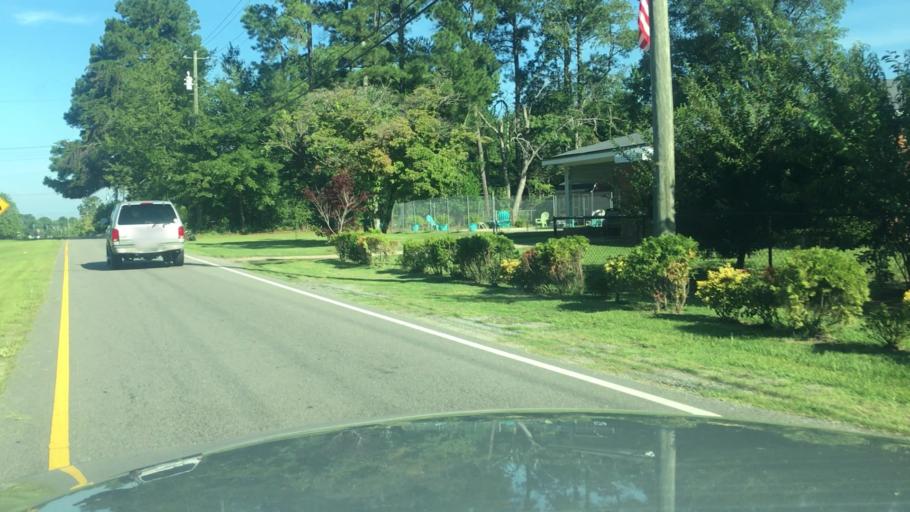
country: US
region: North Carolina
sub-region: Cumberland County
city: Fayetteville
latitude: 35.1305
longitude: -78.8806
